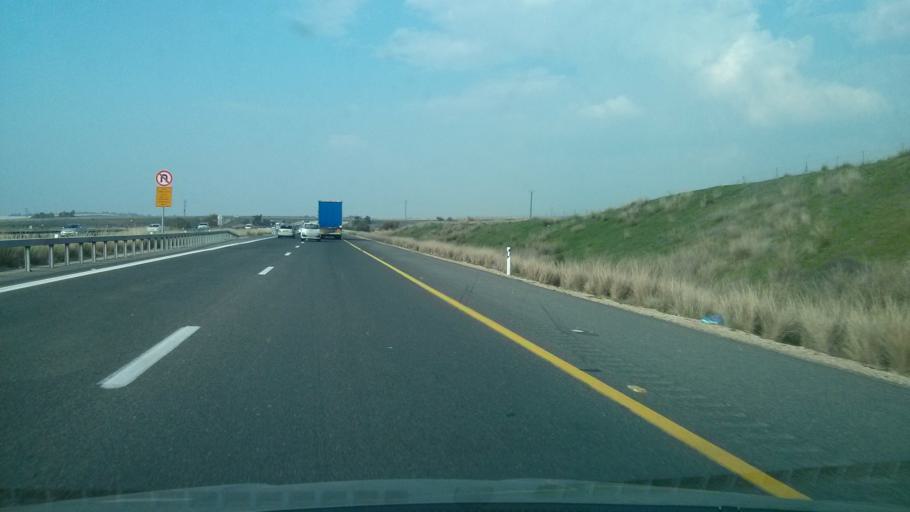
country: IL
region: Central District
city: Bene 'Ayish
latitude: 31.7390
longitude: 34.8224
